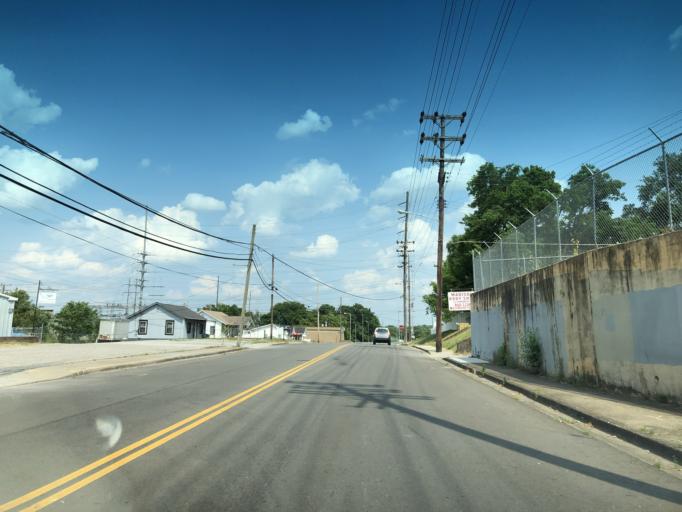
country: US
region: Tennessee
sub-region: Davidson County
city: Goodlettsville
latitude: 36.2607
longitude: -86.7169
